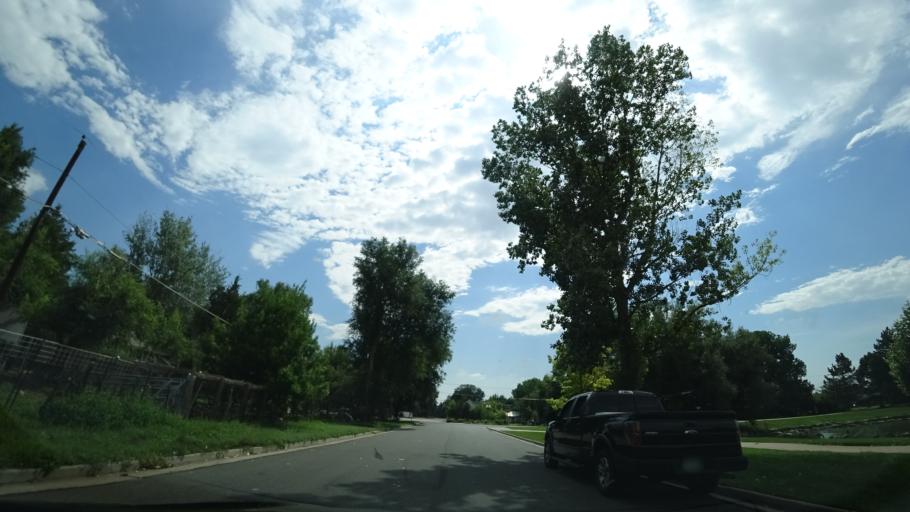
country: US
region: Colorado
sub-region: Jefferson County
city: Lakewood
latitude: 39.7202
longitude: -105.0707
